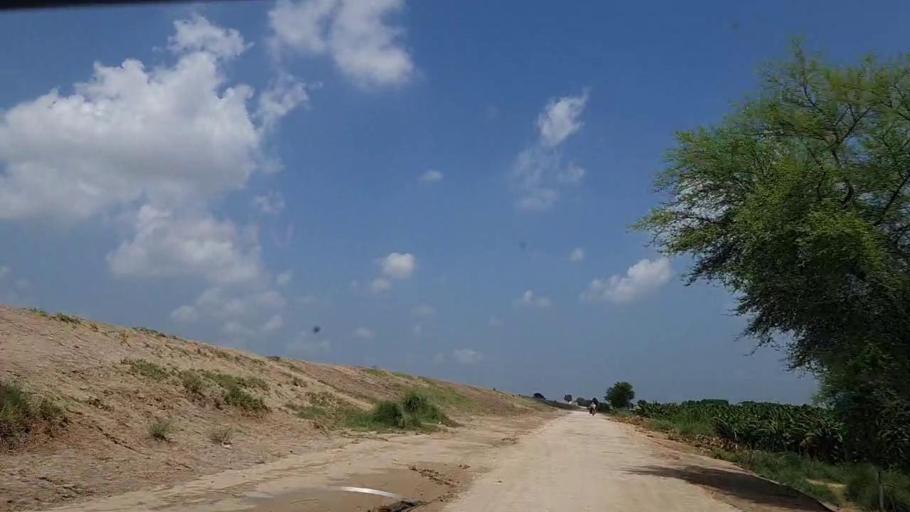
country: PK
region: Sindh
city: Tharu Shah
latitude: 26.9889
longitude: 68.0631
